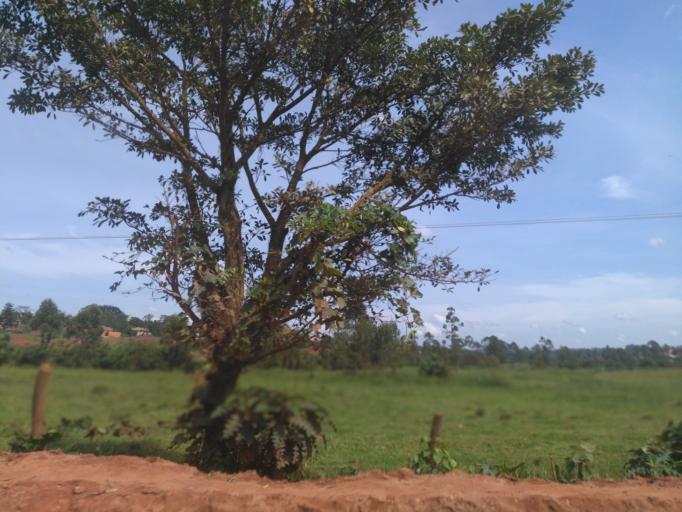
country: UG
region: Central Region
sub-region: Wakiso District
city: Kireka
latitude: 0.4409
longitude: 32.5953
